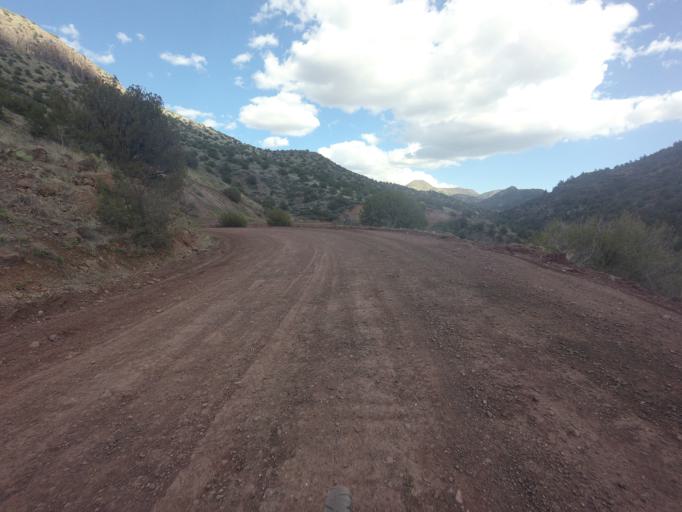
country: US
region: Arizona
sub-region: Yavapai County
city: Camp Verde
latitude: 34.4530
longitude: -111.6988
